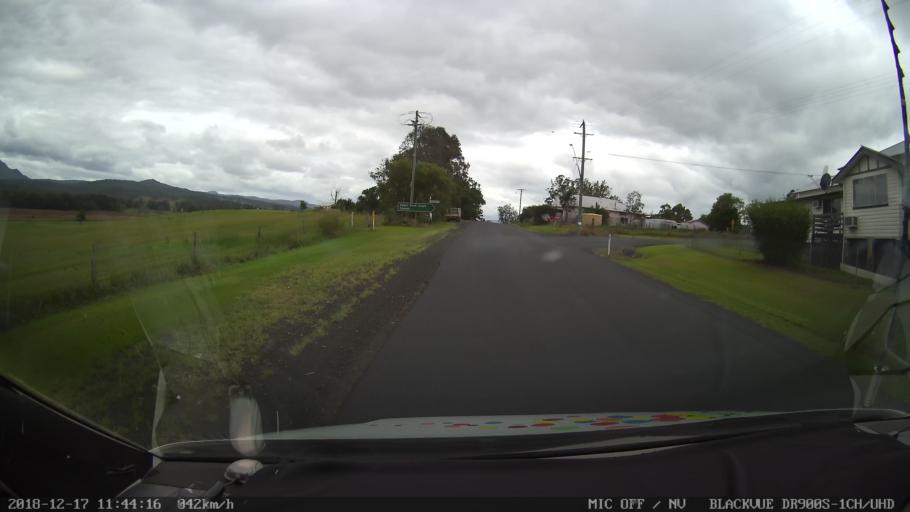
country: AU
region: New South Wales
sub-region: Kyogle
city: Kyogle
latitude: -28.6542
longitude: 152.5950
